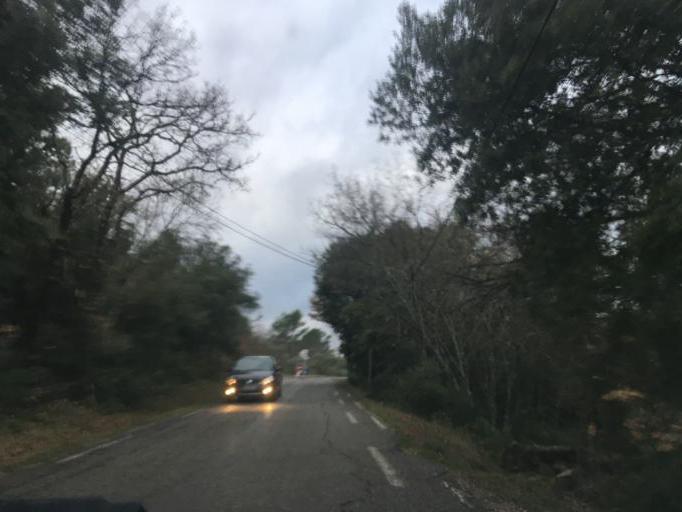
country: FR
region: Provence-Alpes-Cote d'Azur
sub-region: Departement du Var
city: Flassans-sur-Issole
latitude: 43.3655
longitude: 6.2076
